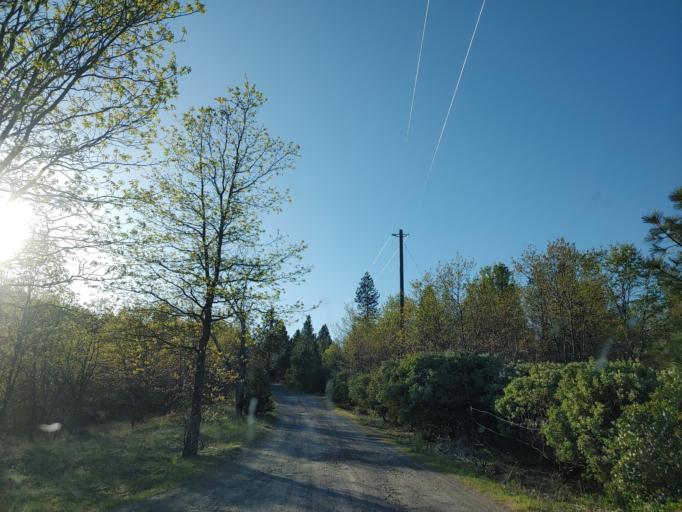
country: US
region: California
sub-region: Shasta County
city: Burney
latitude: 40.8109
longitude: -121.9441
